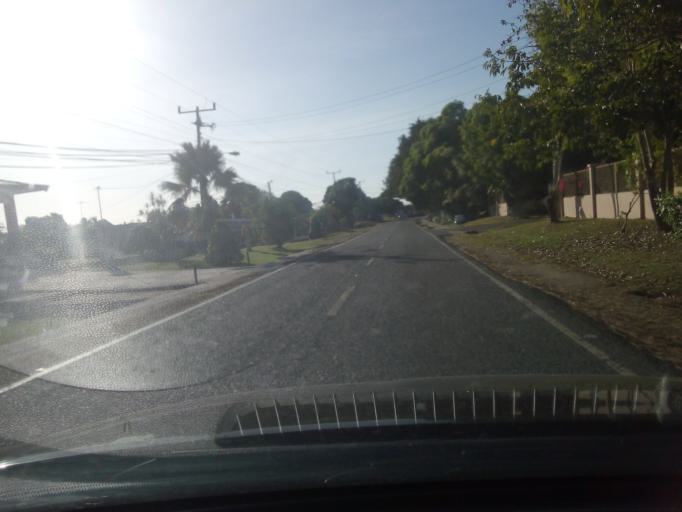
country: PA
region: Veraguas
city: Atalaya
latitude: 8.0462
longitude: -80.9295
